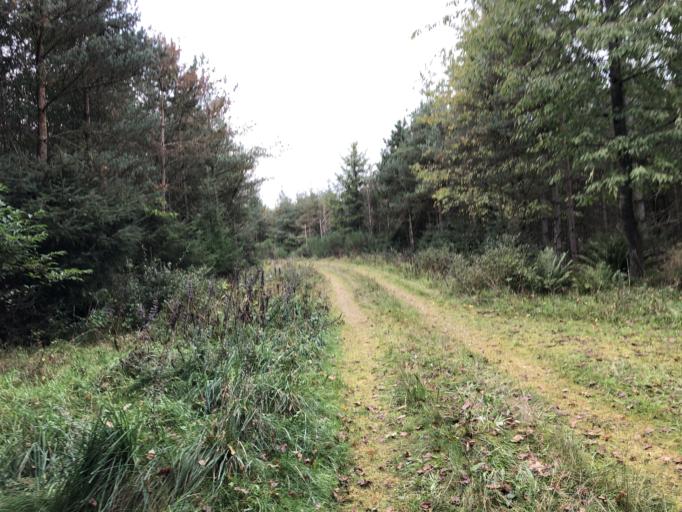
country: DK
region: Central Jutland
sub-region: Holstebro Kommune
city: Ulfborg
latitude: 56.2166
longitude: 8.4375
